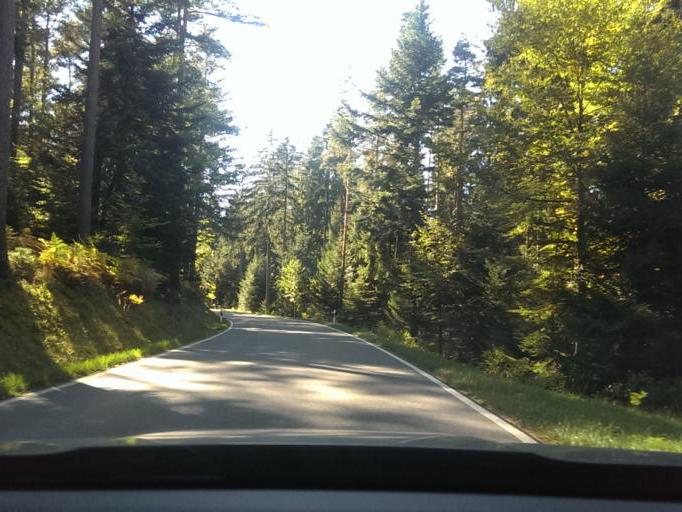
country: DE
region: Baden-Wuerttemberg
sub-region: Karlsruhe Region
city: Enzklosterle
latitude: 48.6822
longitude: 8.5308
